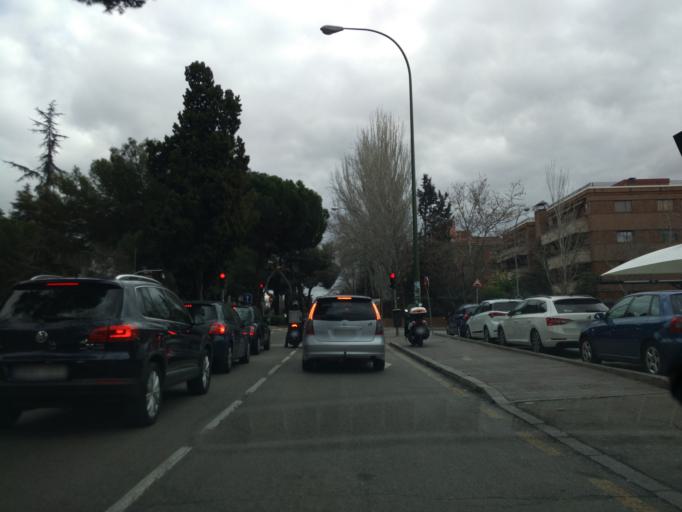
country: ES
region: Madrid
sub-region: Provincia de Madrid
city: Ciudad Lineal
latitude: 40.4576
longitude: -3.6582
